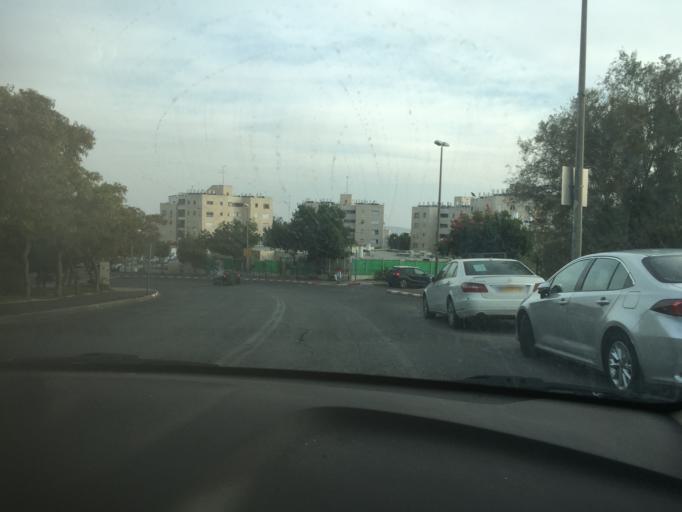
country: IL
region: Jerusalem
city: Jerusalem
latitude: 31.7464
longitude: 35.2315
